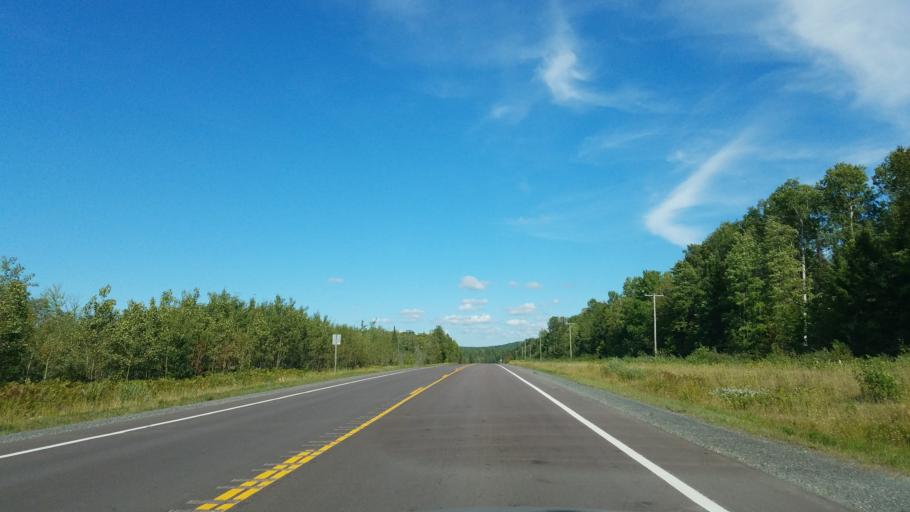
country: US
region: Michigan
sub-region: Baraga County
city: Baraga
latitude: 46.5142
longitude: -88.6728
